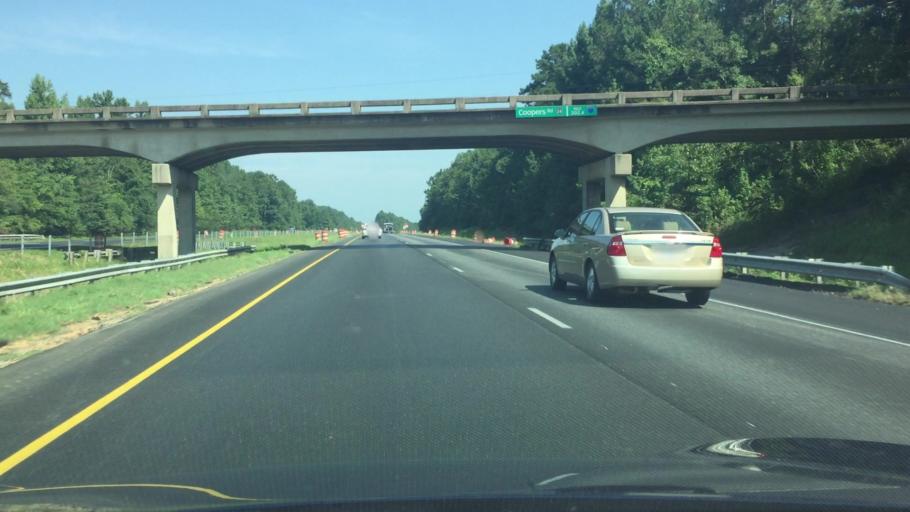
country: US
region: Alabama
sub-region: Chilton County
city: Clanton
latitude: 32.7618
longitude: -86.5601
